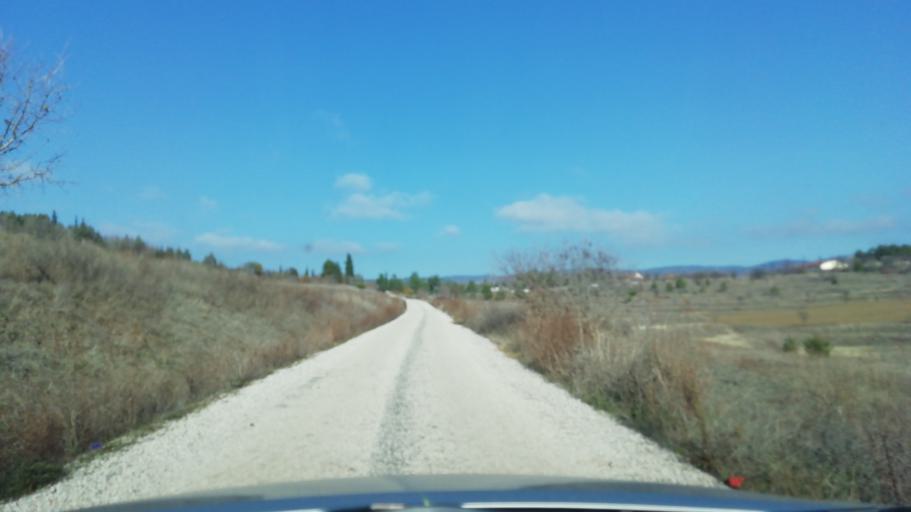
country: TR
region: Karabuk
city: Safranbolu
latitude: 41.2274
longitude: 32.7762
